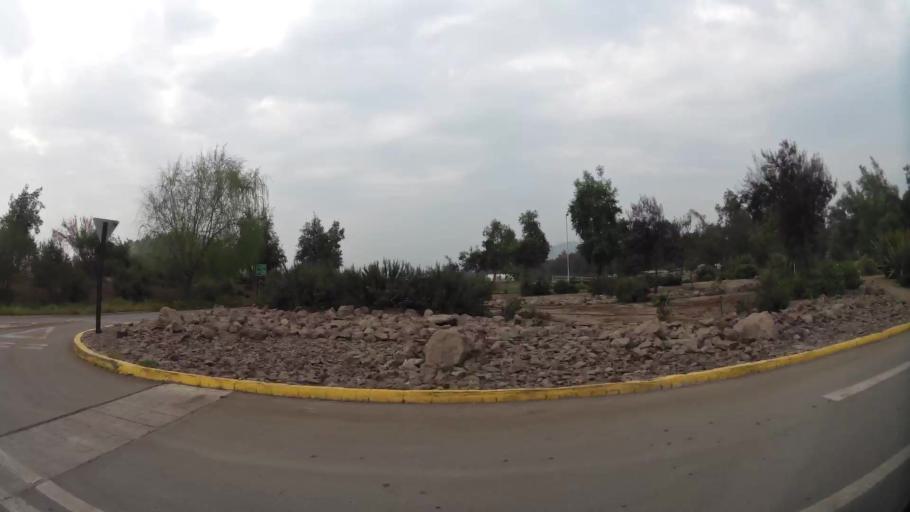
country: CL
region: Santiago Metropolitan
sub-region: Provincia de Chacabuco
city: Chicureo Abajo
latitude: -33.2001
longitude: -70.6602
